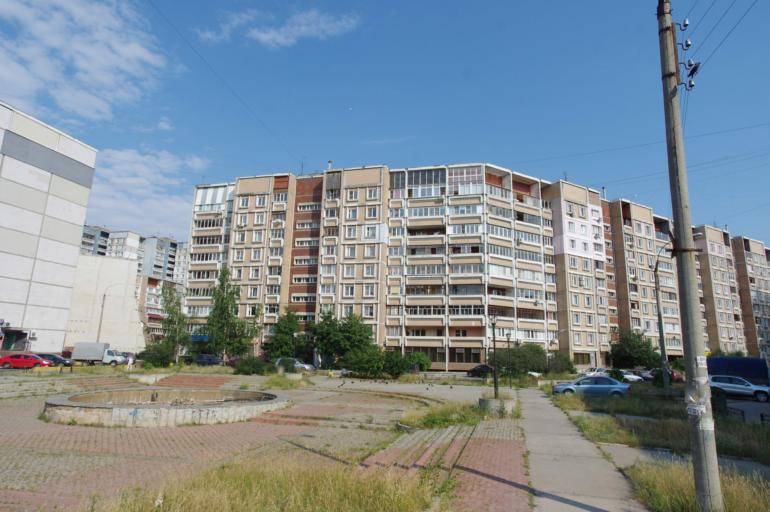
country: RU
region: Nizjnij Novgorod
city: Nizhniy Novgorod
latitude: 56.3447
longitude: 43.9377
